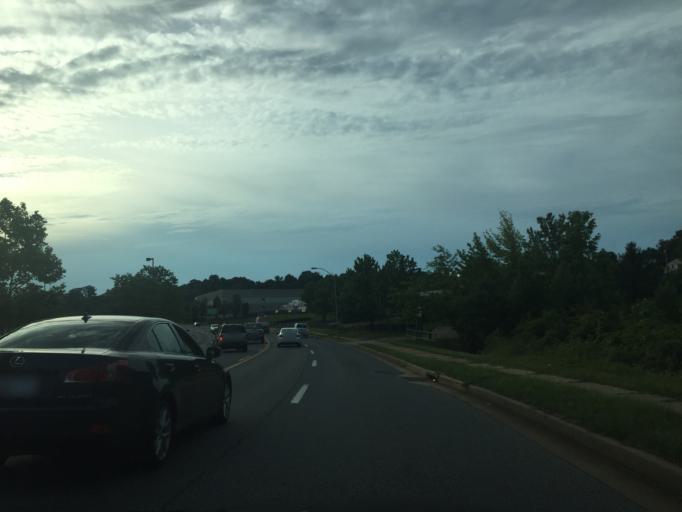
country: US
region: Maryland
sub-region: Baltimore County
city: Overlea
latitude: 39.3713
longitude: -76.5046
